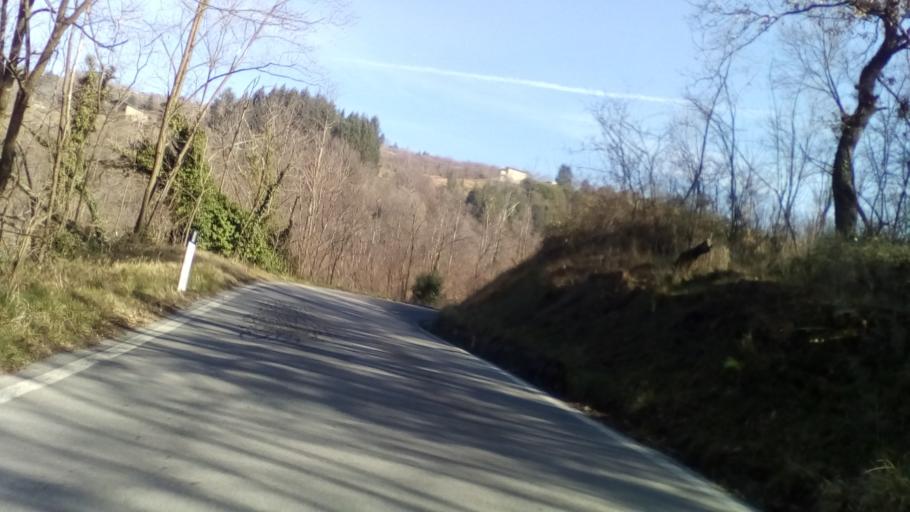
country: IT
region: Tuscany
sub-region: Provincia di Lucca
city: Castiglione di Garfagnana
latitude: 44.1423
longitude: 10.4266
